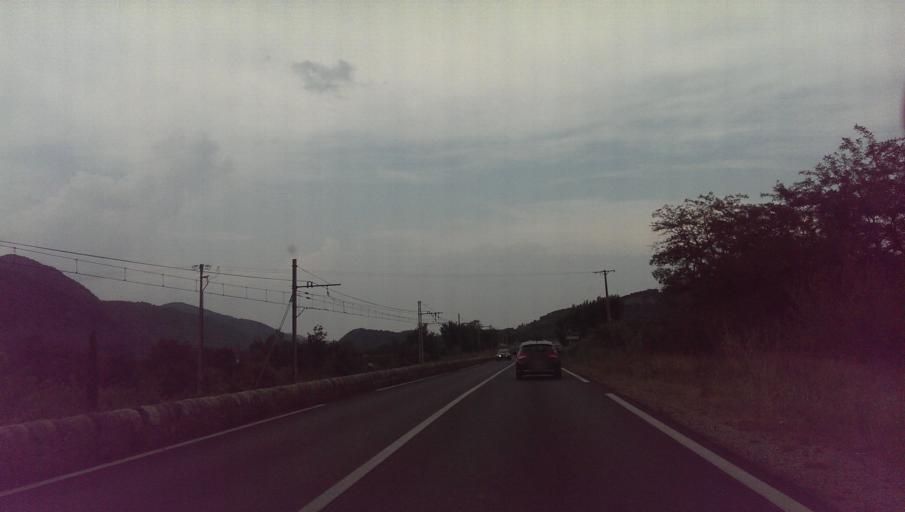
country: FR
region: Languedoc-Roussillon
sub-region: Departement des Pyrenees-Orientales
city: Vinca
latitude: 42.6442
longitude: 2.4987
